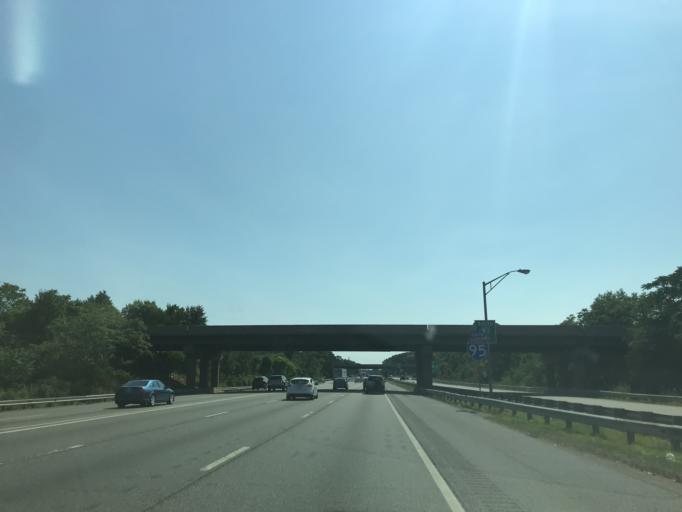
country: US
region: Delaware
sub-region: New Castle County
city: Newport
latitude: 39.7047
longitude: -75.6027
